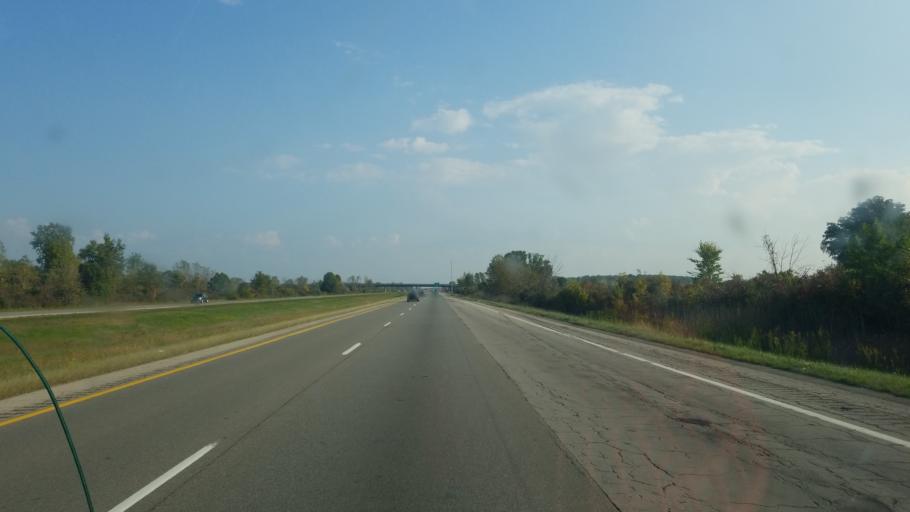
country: US
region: Michigan
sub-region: Monroe County
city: Carleton
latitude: 42.0129
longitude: -83.3430
